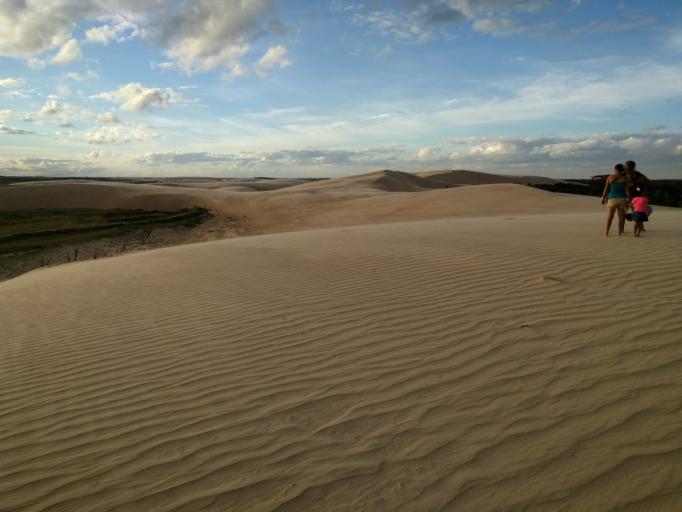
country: BO
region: Santa Cruz
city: Cotoca
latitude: -17.9727
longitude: -63.1452
